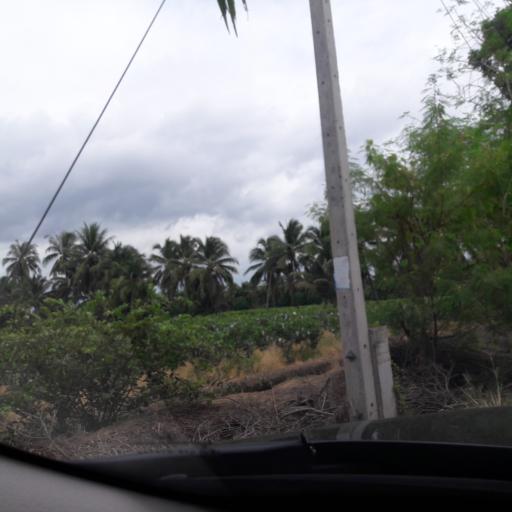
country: TH
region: Ratchaburi
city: Damnoen Saduak
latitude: 13.5702
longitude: 99.9514
